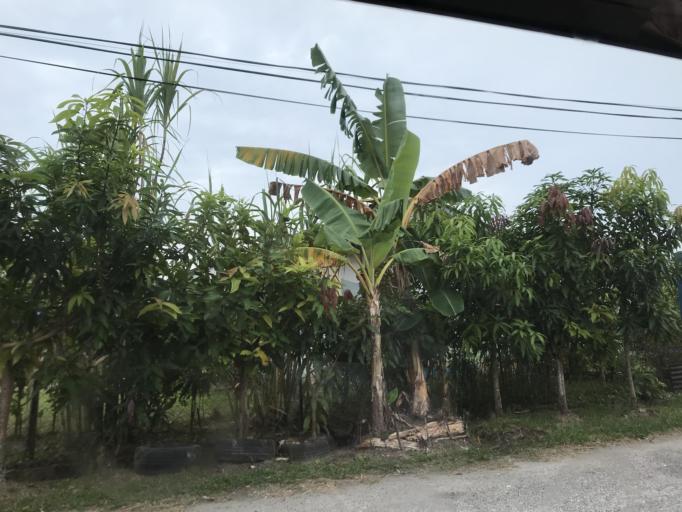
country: MY
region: Kelantan
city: Kota Bharu
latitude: 6.1147
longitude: 102.2114
